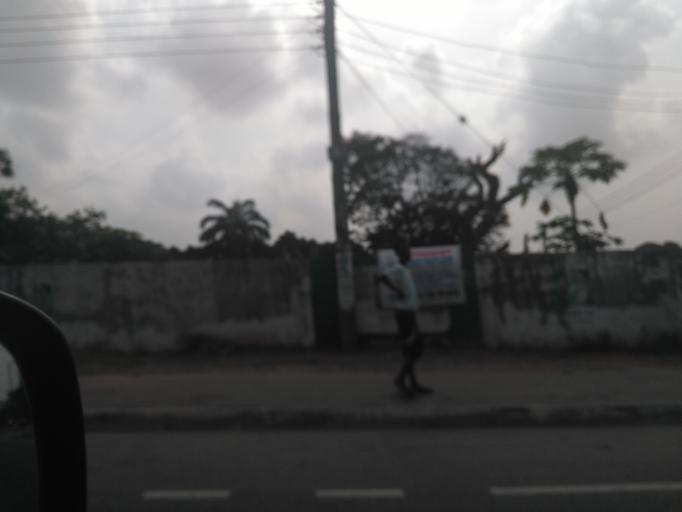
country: GH
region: Greater Accra
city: Accra
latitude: 5.5765
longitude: -0.1972
